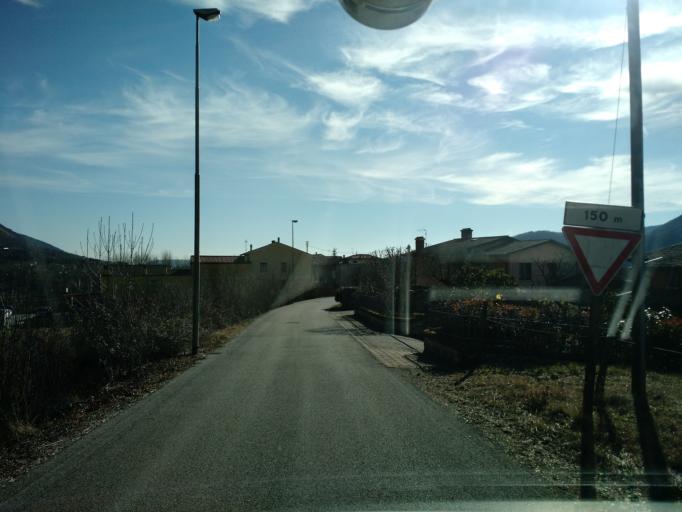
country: IT
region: Veneto
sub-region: Provincia di Vicenza
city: Cogollo del Cengio
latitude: 45.7923
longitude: 11.4045
